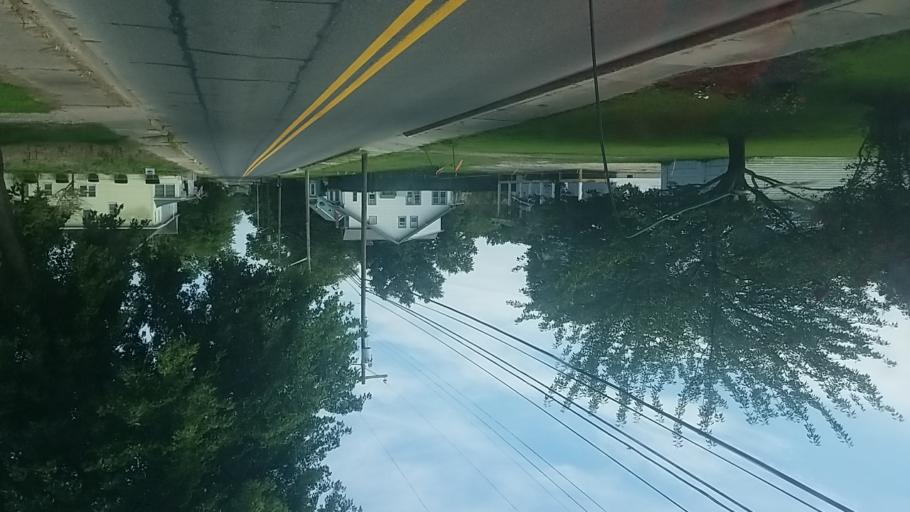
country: US
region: Delaware
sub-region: Sussex County
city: Selbyville
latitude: 38.5189
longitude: -75.2288
